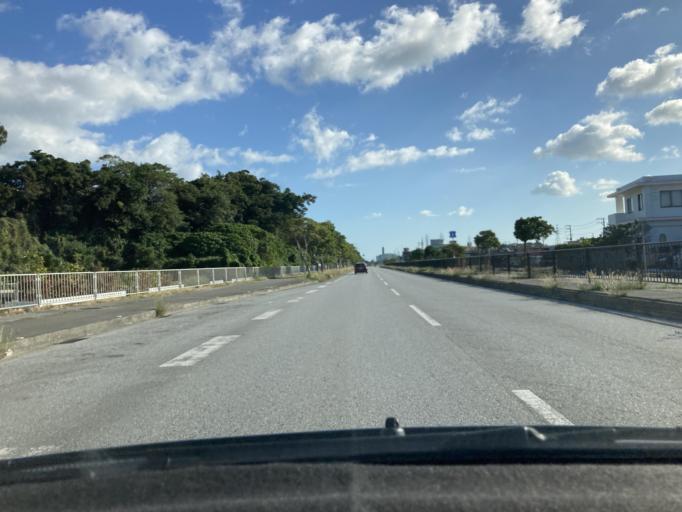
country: JP
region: Okinawa
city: Ishikawa
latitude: 26.4141
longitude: 127.8178
